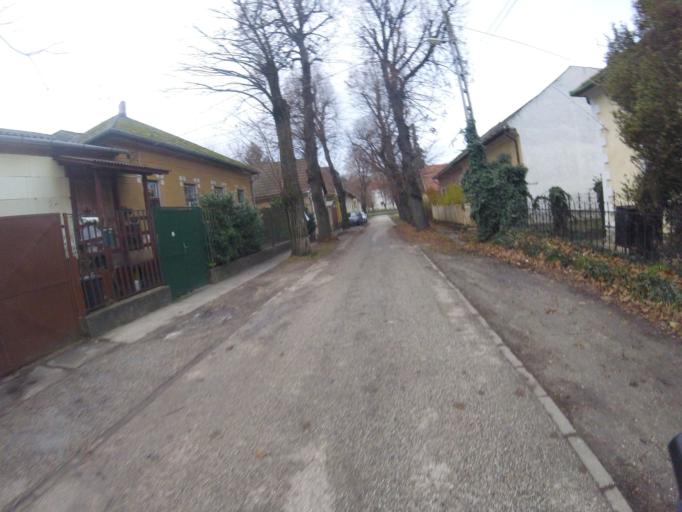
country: HU
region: Pest
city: Budakalasz
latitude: 47.6183
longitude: 19.0538
